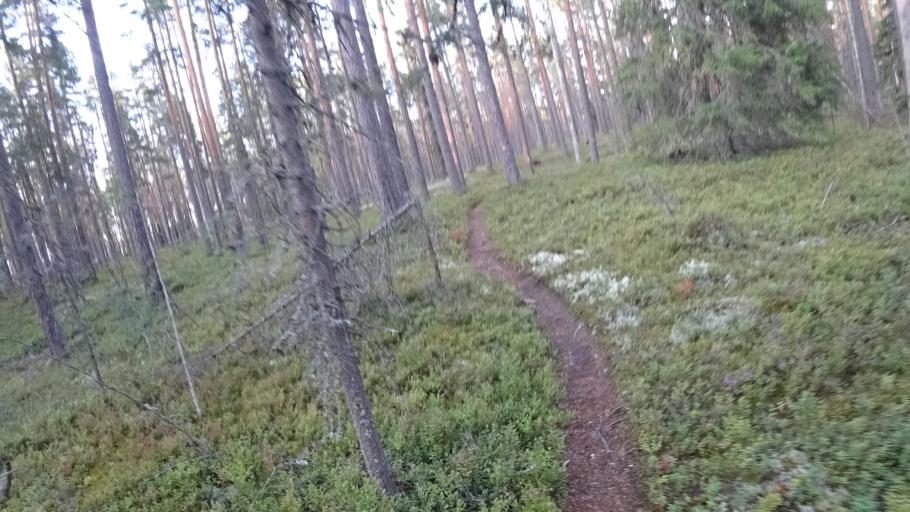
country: FI
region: North Karelia
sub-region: Joensuu
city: Ilomantsi
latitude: 62.5809
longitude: 31.1747
